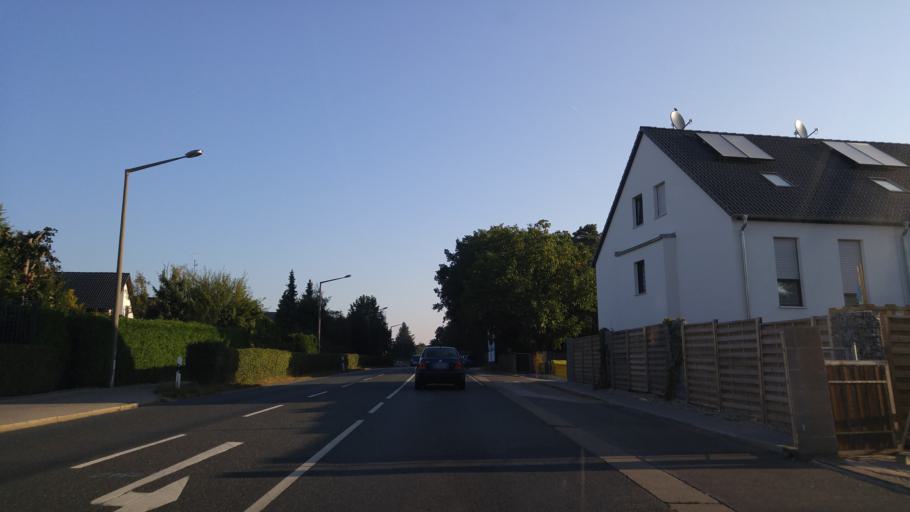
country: DE
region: Bavaria
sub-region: Regierungsbezirk Mittelfranken
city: Furth
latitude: 49.5249
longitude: 10.9773
